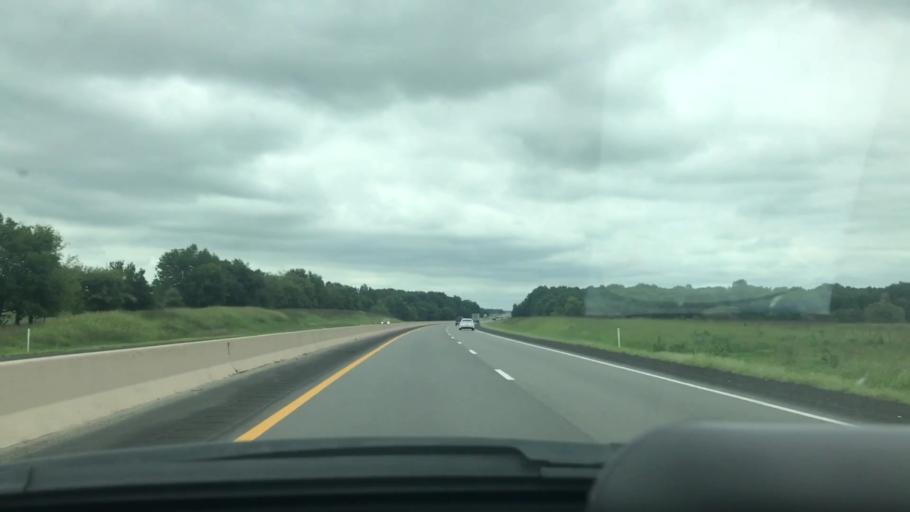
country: US
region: Oklahoma
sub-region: Craig County
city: Vinita
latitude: 36.6570
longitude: -95.0994
